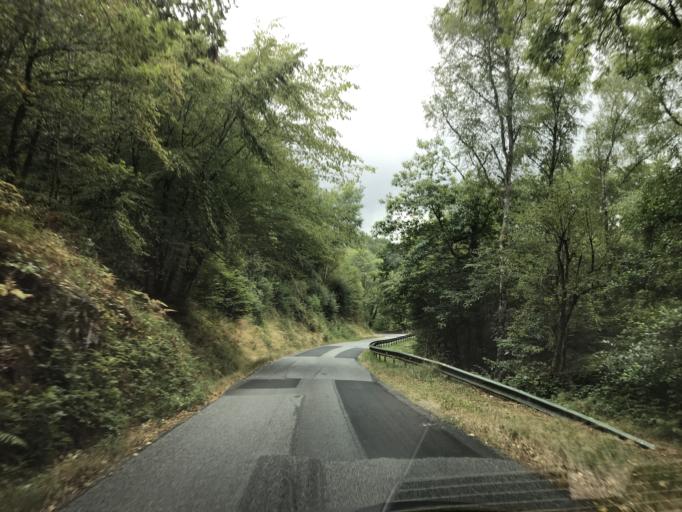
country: FR
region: Auvergne
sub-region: Departement du Cantal
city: Pleaux
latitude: 45.2409
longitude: 2.1817
